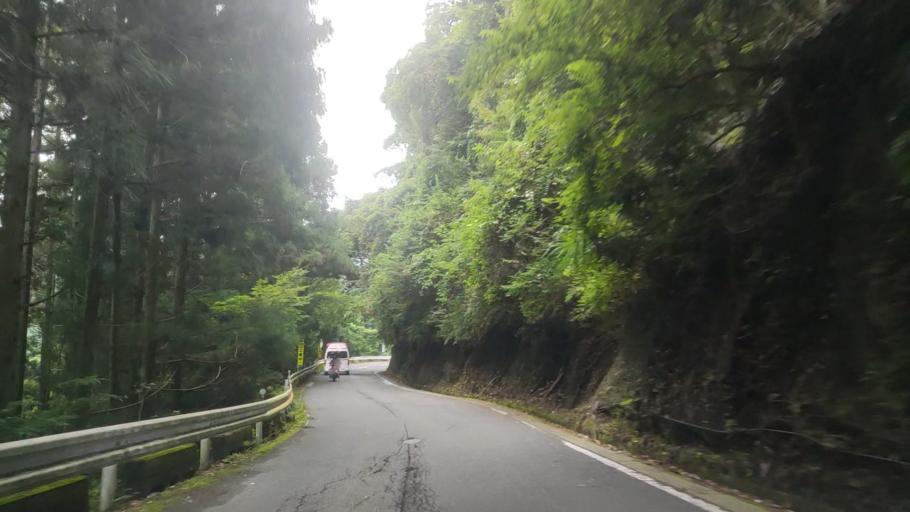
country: JP
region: Wakayama
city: Koya
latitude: 34.2265
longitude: 135.5403
